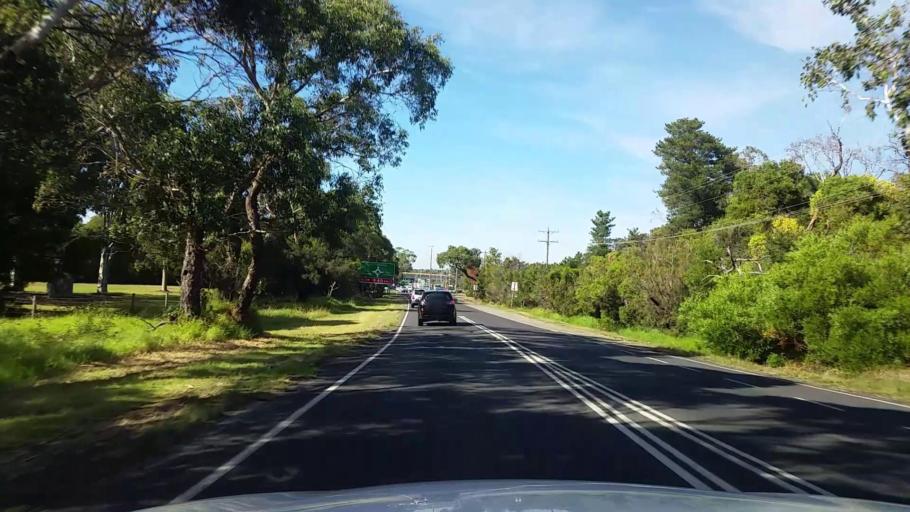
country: AU
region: Victoria
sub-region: Mornington Peninsula
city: Baxter
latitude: -38.1922
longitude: 145.1470
